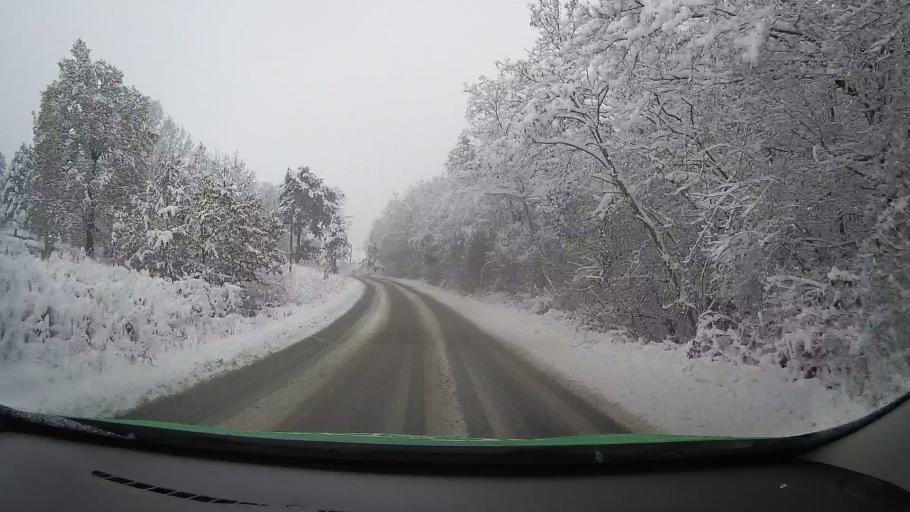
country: RO
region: Hunedoara
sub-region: Comuna Teliucu Inferior
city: Teliucu Inferior
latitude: 45.7062
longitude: 22.8820
